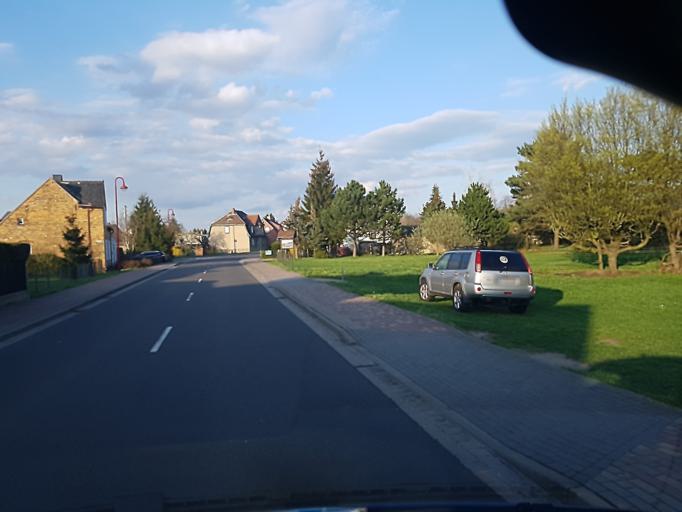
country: DE
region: Saxony
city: Lobnitz
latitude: 51.6169
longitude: 12.4941
